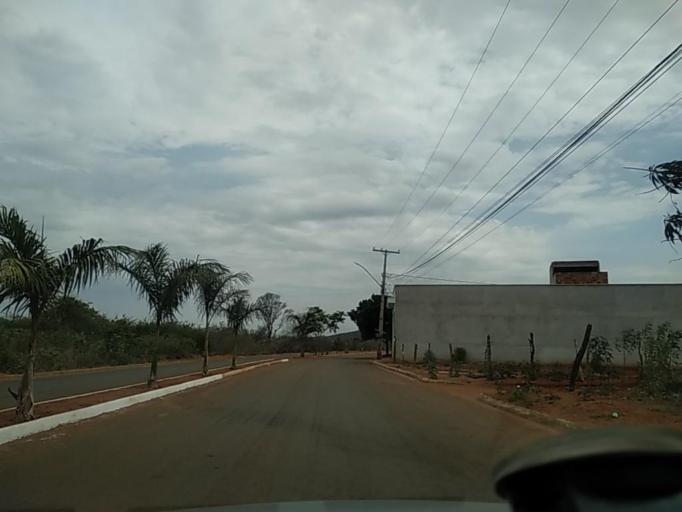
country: BR
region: Bahia
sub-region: Caetite
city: Caetite
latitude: -14.0548
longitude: -42.4720
